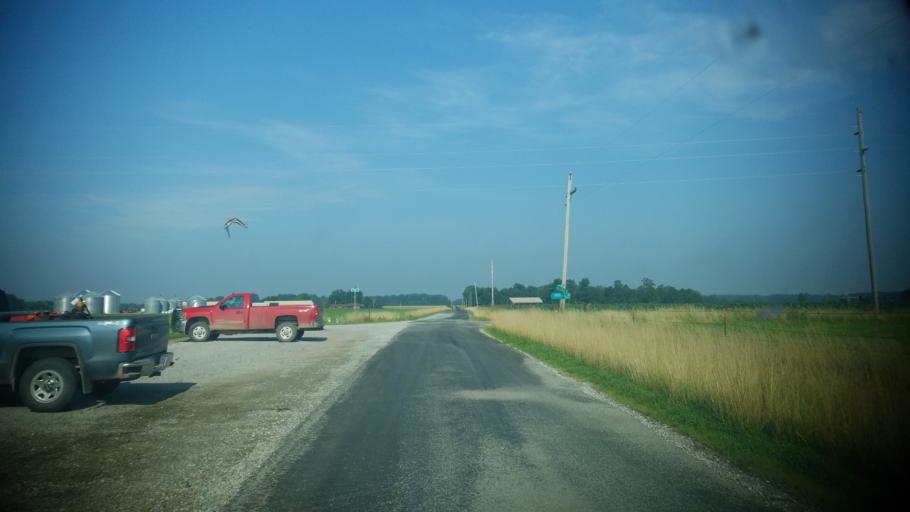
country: US
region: Illinois
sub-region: Clay County
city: Flora
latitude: 38.6024
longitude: -88.3822
